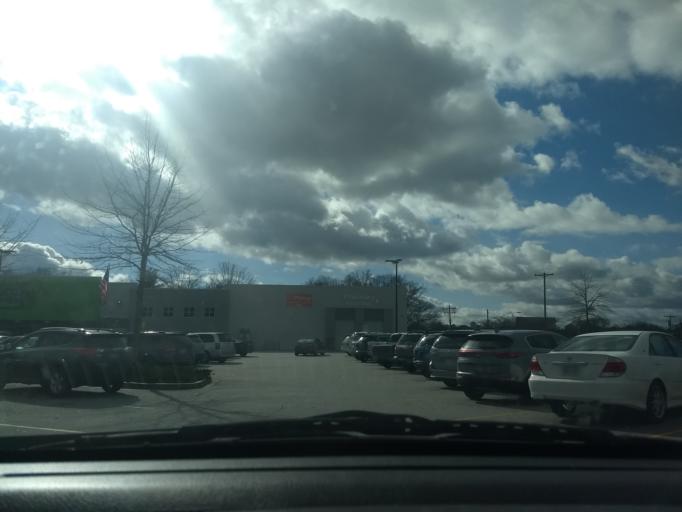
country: US
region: South Carolina
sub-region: Greenville County
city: Wade Hampton
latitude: 34.8842
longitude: -82.3539
